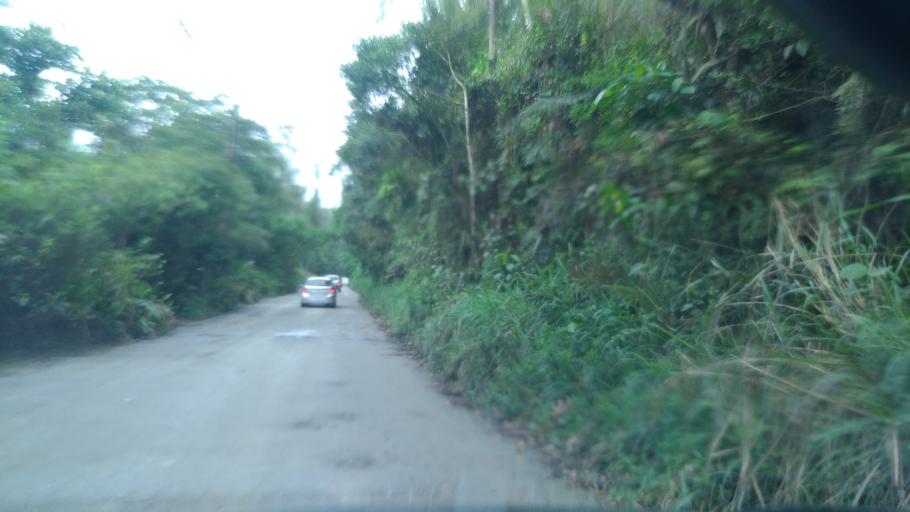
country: BR
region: Sao Paulo
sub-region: Sao Bernardo Do Campo
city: Sao Bernardo do Campo
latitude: -23.7412
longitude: -46.5120
